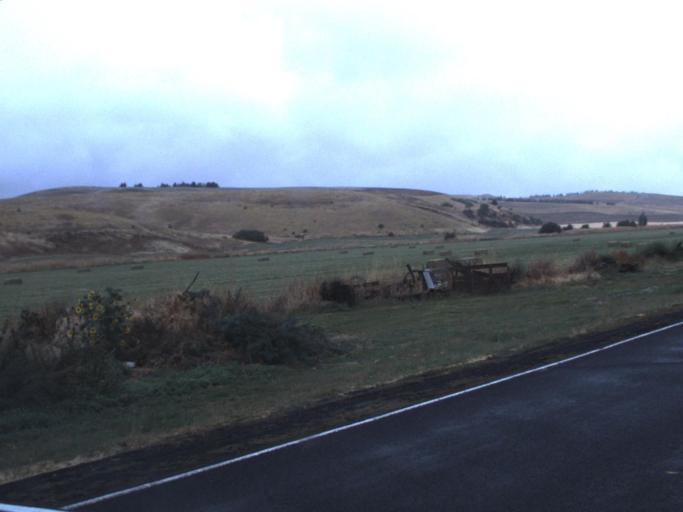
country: US
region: Washington
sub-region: Whitman County
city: Colfax
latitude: 47.0436
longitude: -117.5140
